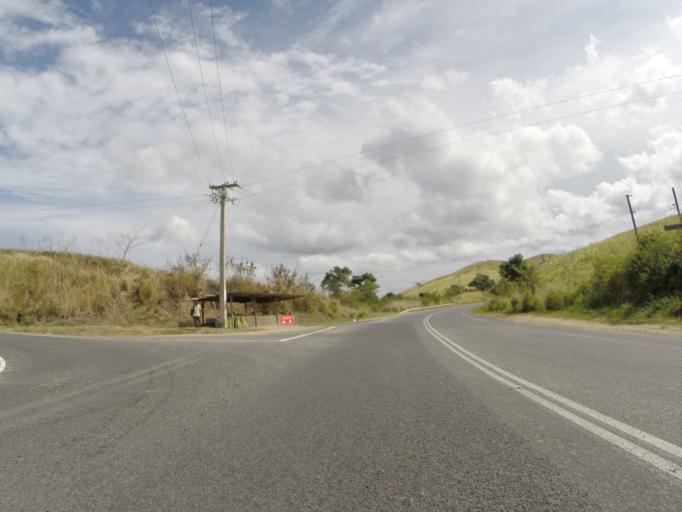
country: FJ
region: Western
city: Nadi
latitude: -18.1026
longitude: 177.3985
